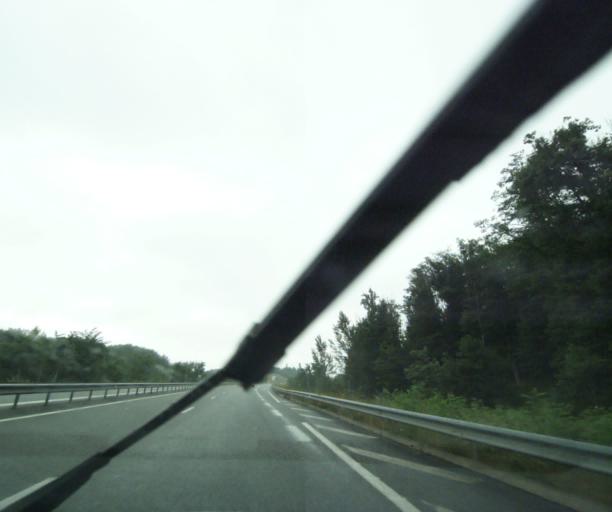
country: FR
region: Midi-Pyrenees
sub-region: Departement du Tarn
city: Le Garric
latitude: 43.9999
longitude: 2.1717
